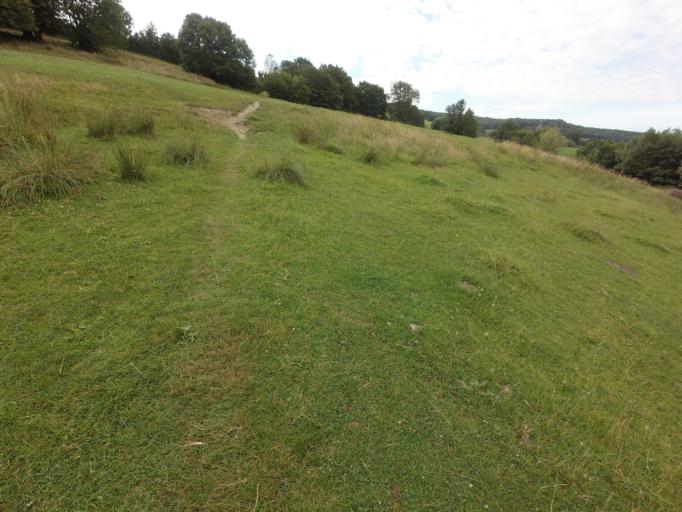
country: BE
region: Wallonia
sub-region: Province de Liege
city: Plombieres
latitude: 50.7569
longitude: 5.9126
